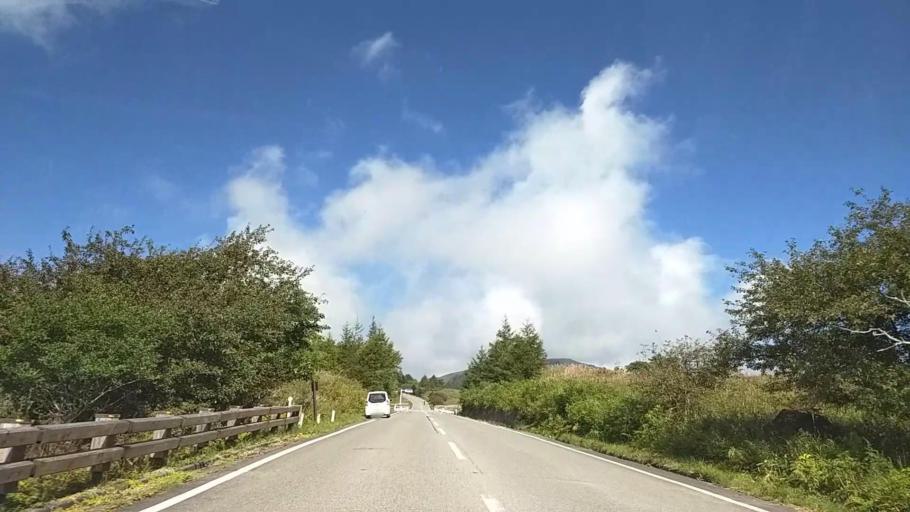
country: JP
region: Nagano
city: Suwa
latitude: 36.1131
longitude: 138.1653
